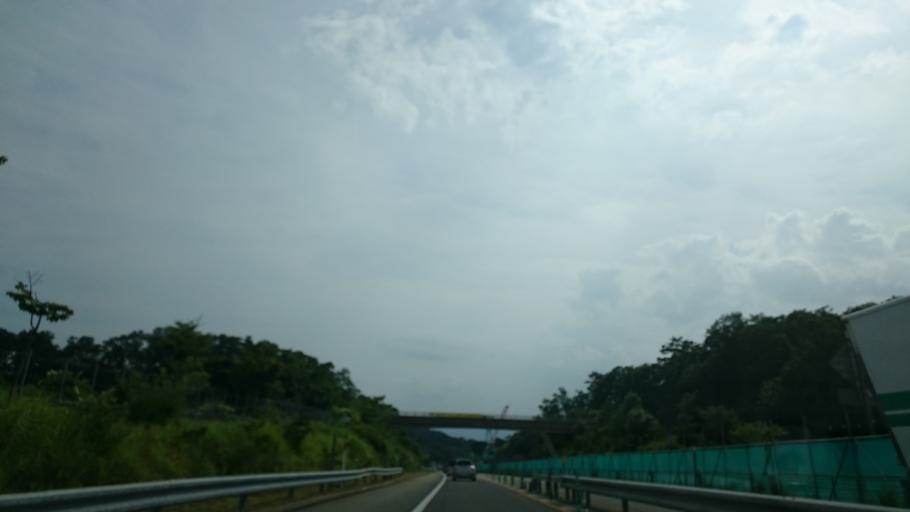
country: JP
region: Gifu
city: Gujo
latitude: 35.9819
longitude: 136.9026
